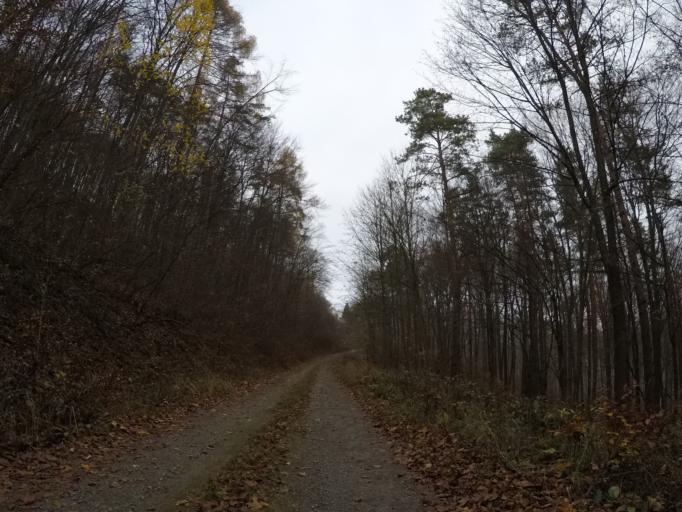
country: SK
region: Presovsky
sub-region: Okres Presov
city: Presov
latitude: 48.8933
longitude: 21.2002
